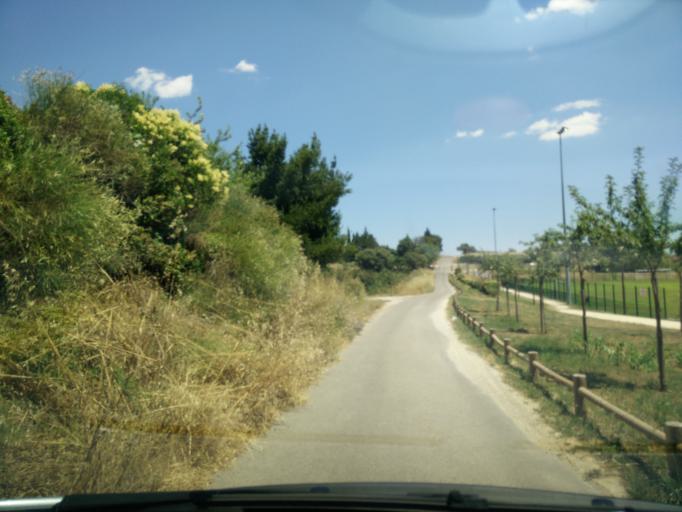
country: FR
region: Languedoc-Roussillon
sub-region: Departement de l'Herault
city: Saint-Christol
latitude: 43.7266
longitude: 4.0819
